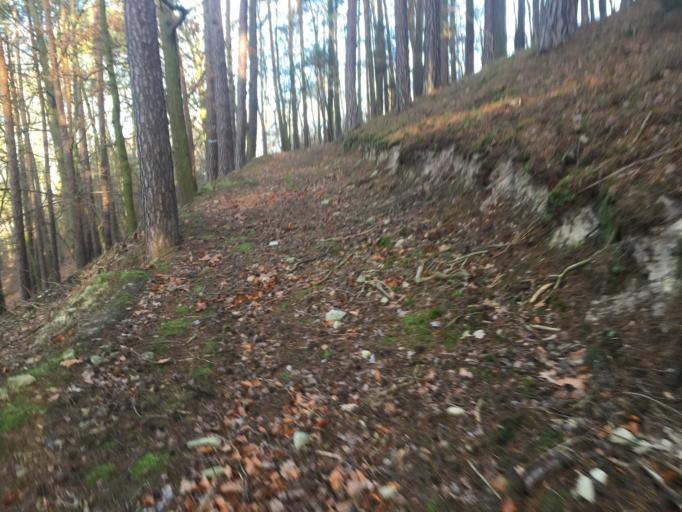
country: DE
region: Thuringia
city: Freienorla
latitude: 50.7579
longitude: 11.5357
